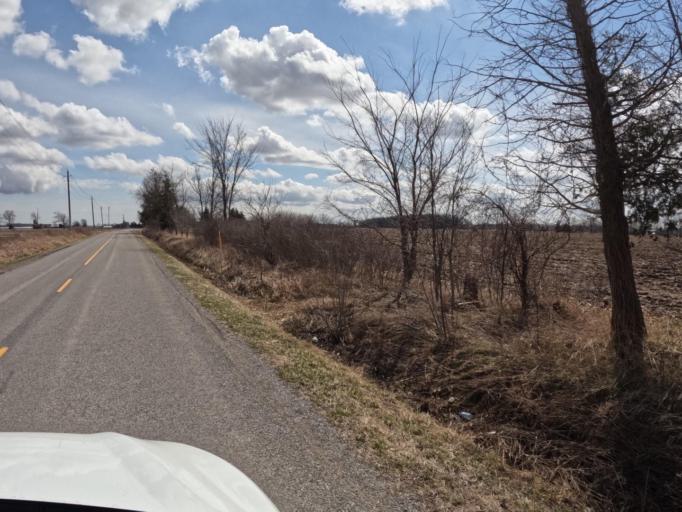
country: CA
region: Ontario
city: Brantford
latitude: 42.9886
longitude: -80.2230
